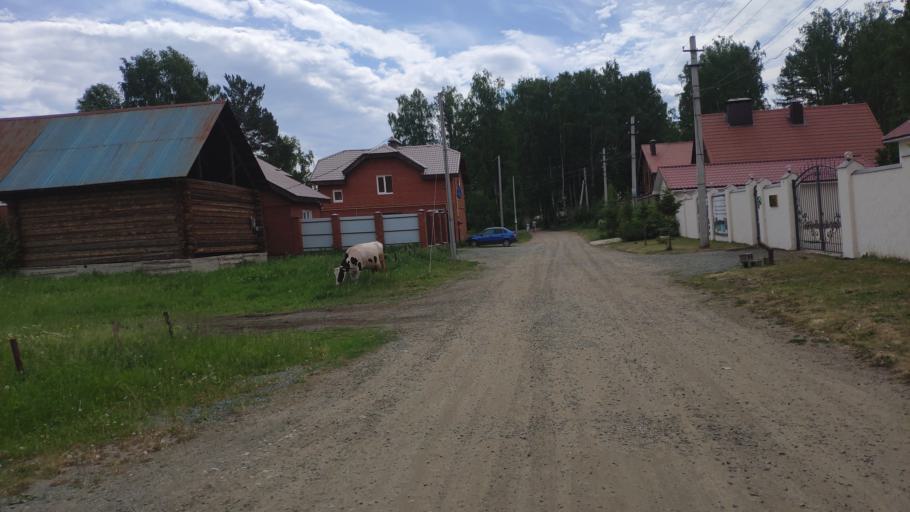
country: RU
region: Bashkortostan
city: Abzakovo
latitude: 53.8136
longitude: 58.6349
